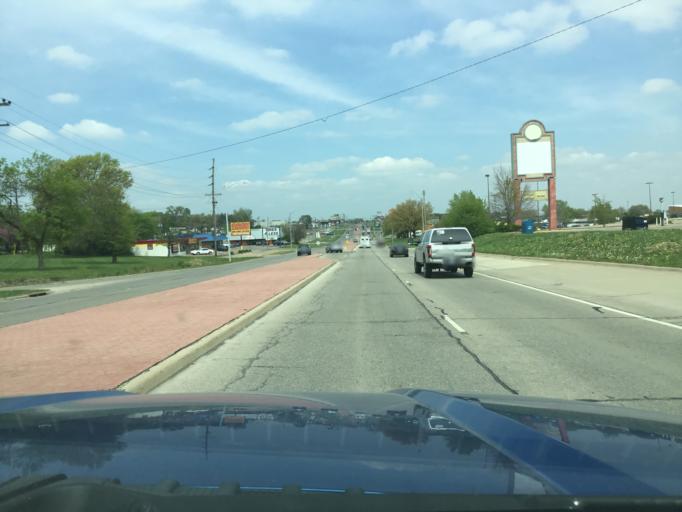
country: US
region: Kansas
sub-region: Shawnee County
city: Topeka
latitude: 39.0020
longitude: -95.6876
